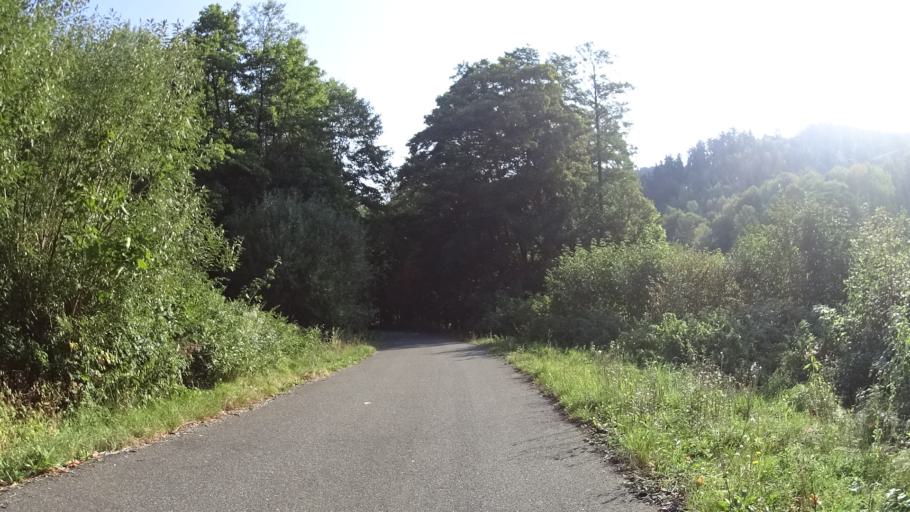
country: CZ
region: Liberecky
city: Hodkovice nad Mohelkou
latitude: 50.6771
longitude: 15.0998
